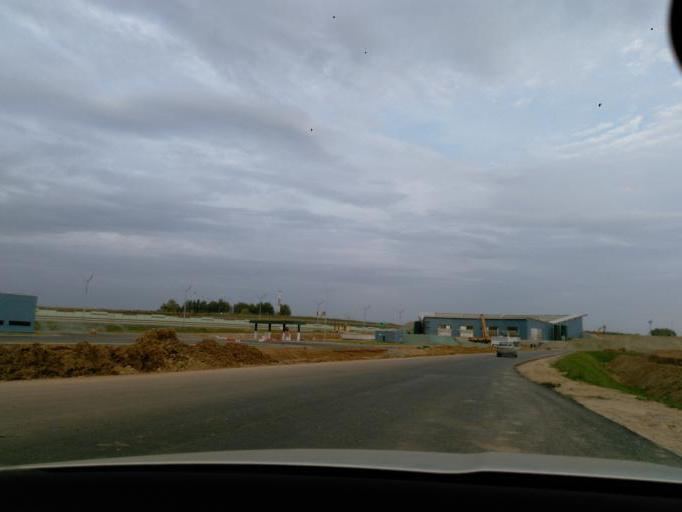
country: RU
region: Moskovskaya
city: Novopodrezkovo
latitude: 55.9598
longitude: 37.3670
